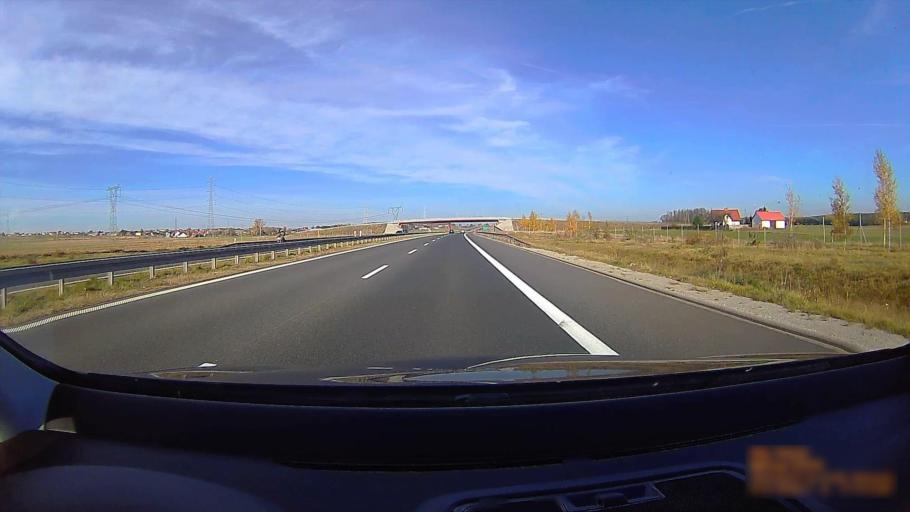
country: PL
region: Greater Poland Voivodeship
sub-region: Powiat ostrowski
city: Przygodzice
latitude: 51.5971
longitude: 17.8512
